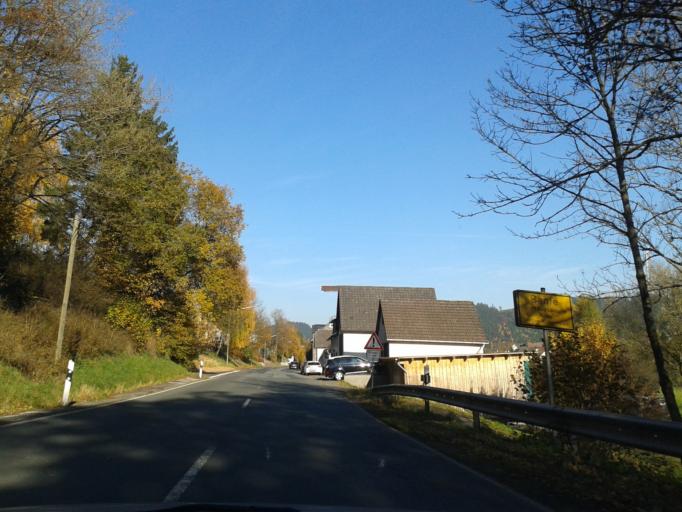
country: DE
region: North Rhine-Westphalia
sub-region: Regierungsbezirk Arnsberg
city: Bad Laasphe
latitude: 50.9087
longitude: 8.3460
